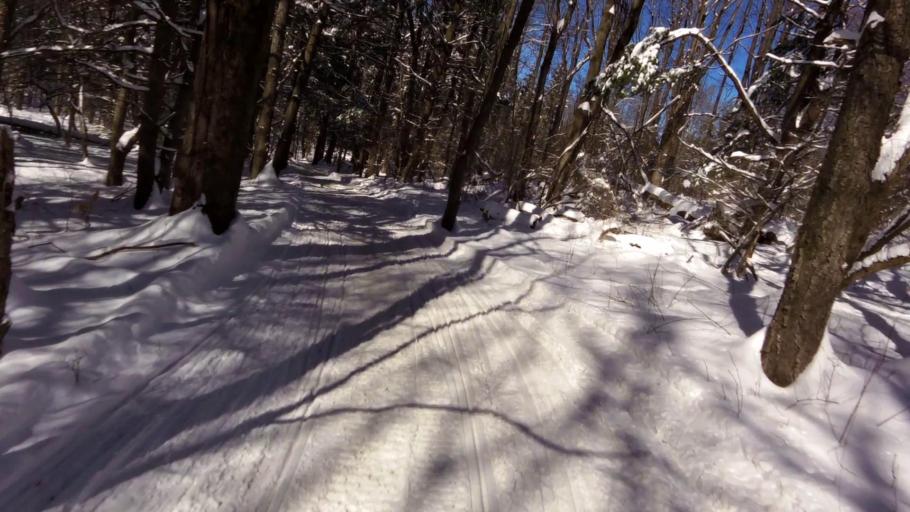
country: US
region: New York
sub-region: Chautauqua County
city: Mayville
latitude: 42.2382
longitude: -79.4223
